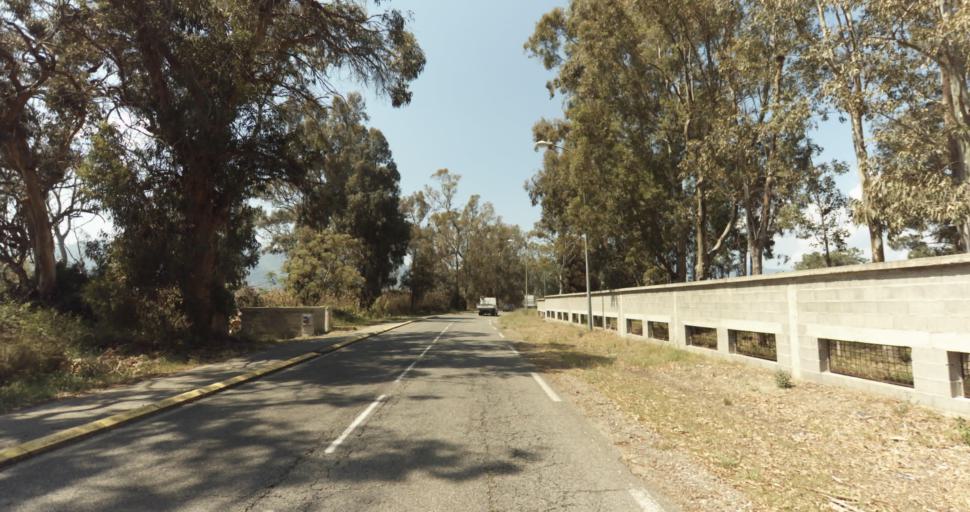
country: FR
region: Corsica
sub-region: Departement de la Haute-Corse
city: Biguglia
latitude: 42.6228
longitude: 9.4723
